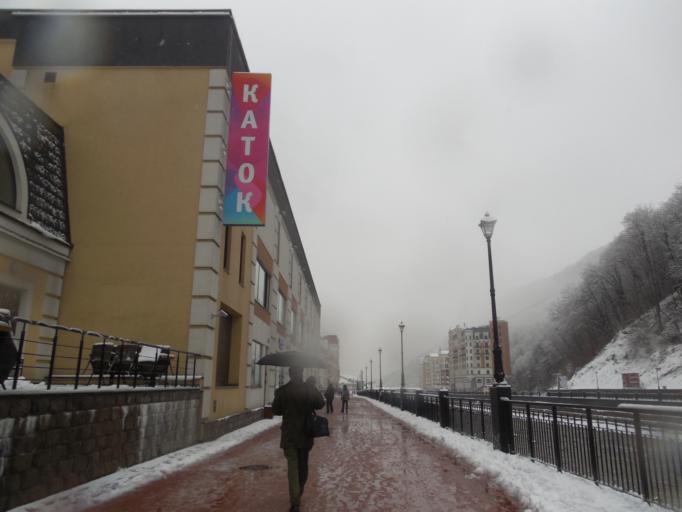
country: RU
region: Krasnodarskiy
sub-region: Sochi City
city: Krasnaya Polyana
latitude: 43.6728
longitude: 40.2914
